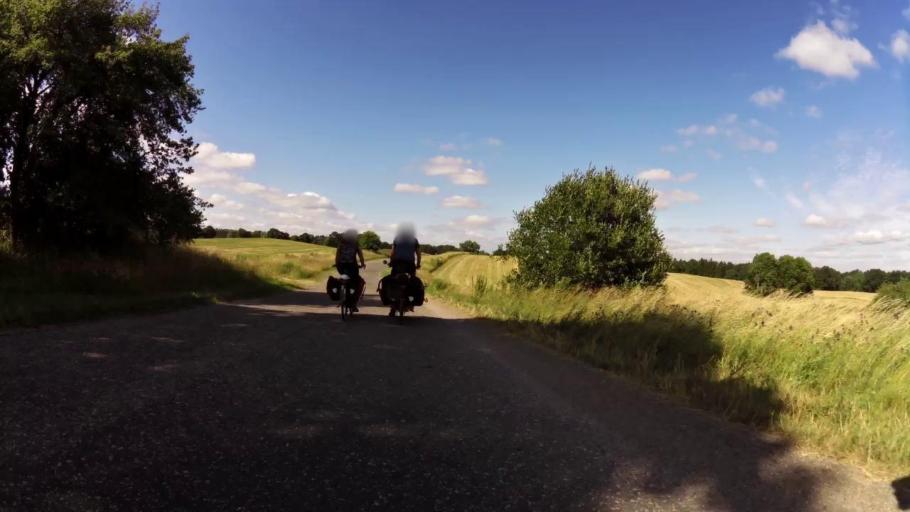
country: PL
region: West Pomeranian Voivodeship
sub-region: Powiat lobeski
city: Lobez
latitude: 53.6471
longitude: 15.6730
